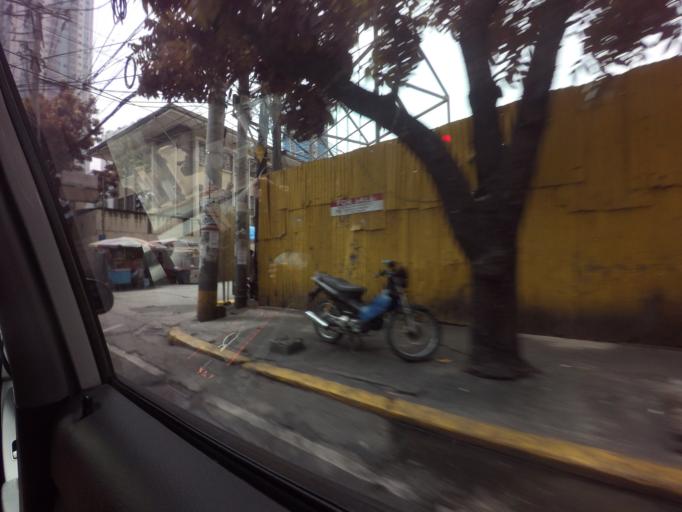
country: PH
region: Metro Manila
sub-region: City of Manila
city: Port Area
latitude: 14.5747
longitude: 120.9852
